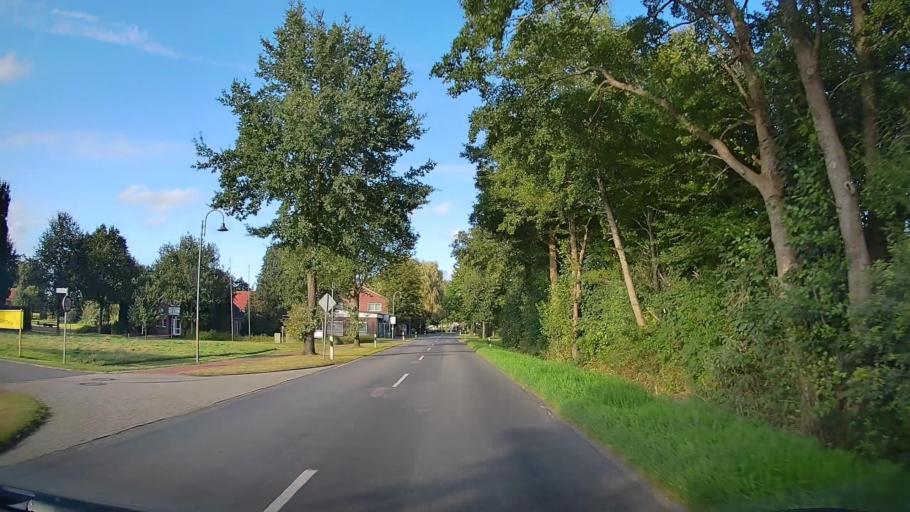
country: DE
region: Lower Saxony
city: Ostrhauderfehn
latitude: 53.1281
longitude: 7.6769
